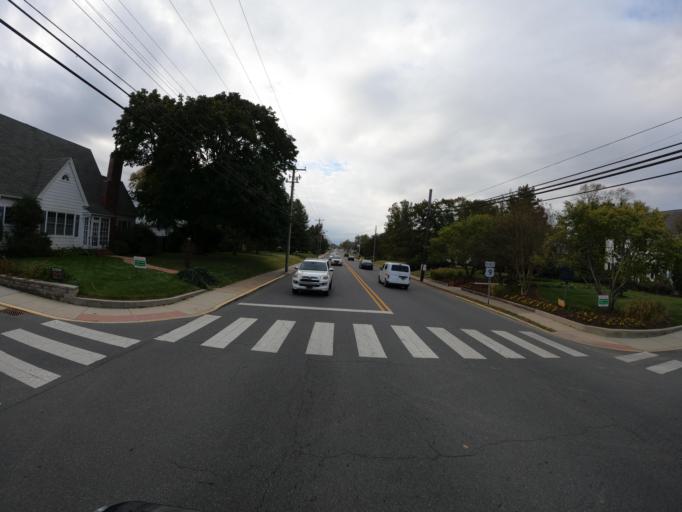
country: US
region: Delaware
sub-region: Sussex County
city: Lewes
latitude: 38.7677
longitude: -75.1463
